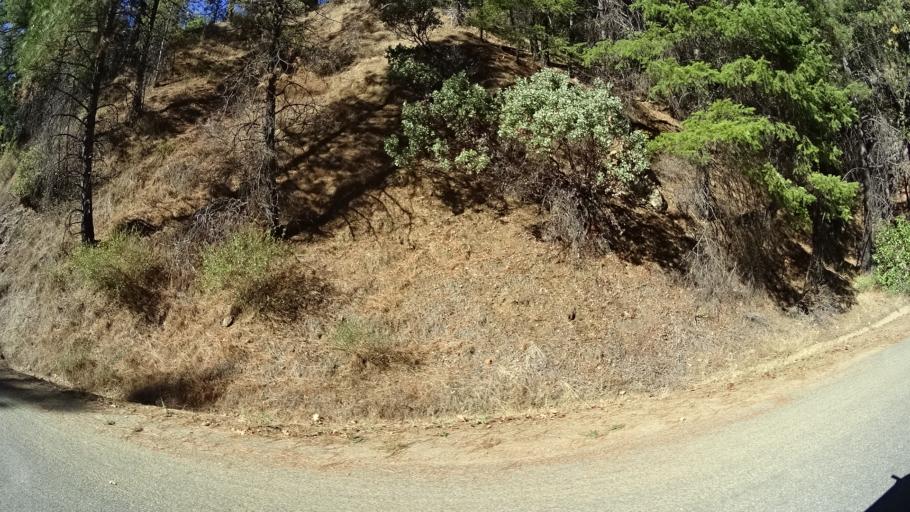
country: US
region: California
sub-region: Siskiyou County
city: Happy Camp
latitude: 41.3105
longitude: -123.1984
